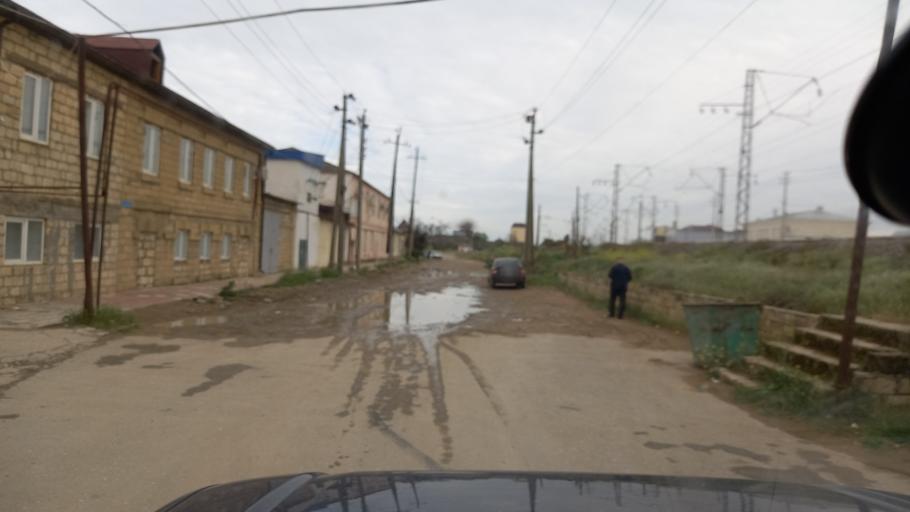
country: RU
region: Dagestan
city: Derbent
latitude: 42.0655
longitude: 48.3035
